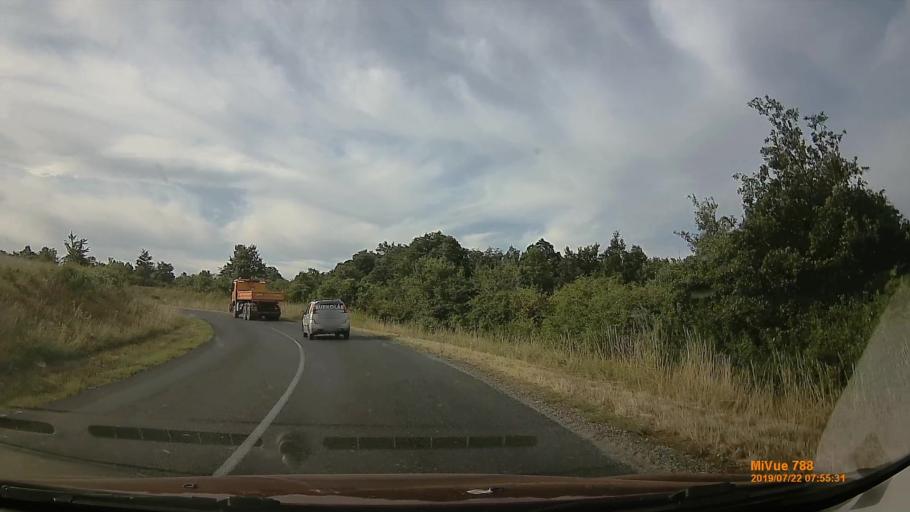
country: HU
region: Veszprem
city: Ajka
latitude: 47.0312
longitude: 17.5575
